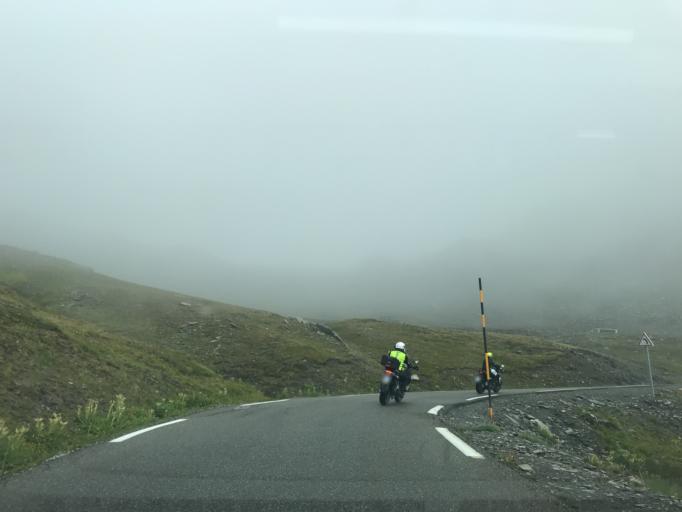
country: IT
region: Piedmont
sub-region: Provincia di Cuneo
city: Pontechianale
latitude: 44.6858
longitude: 6.9789
